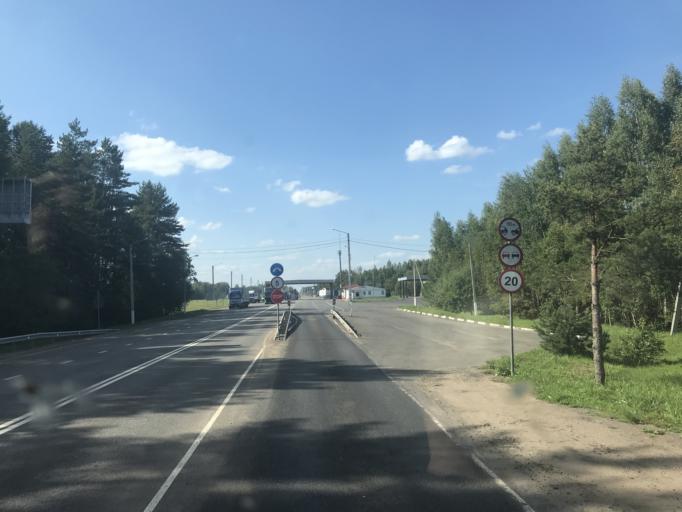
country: RU
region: Smolensk
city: Rudnya
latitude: 54.9871
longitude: 30.9582
